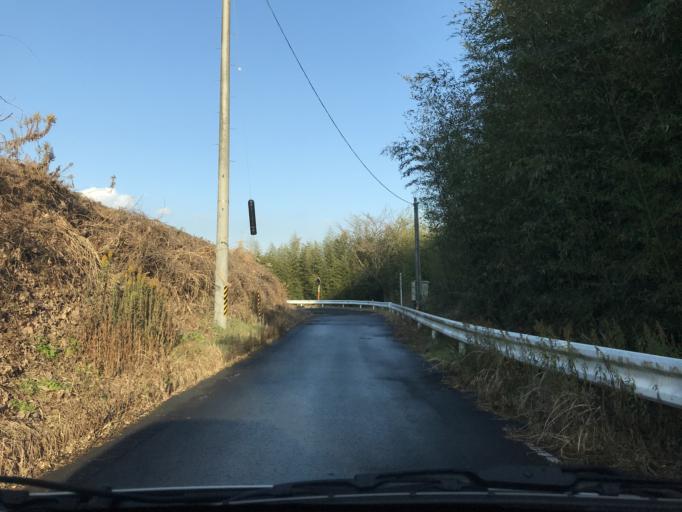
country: JP
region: Miyagi
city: Wakuya
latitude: 38.7004
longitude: 141.1320
